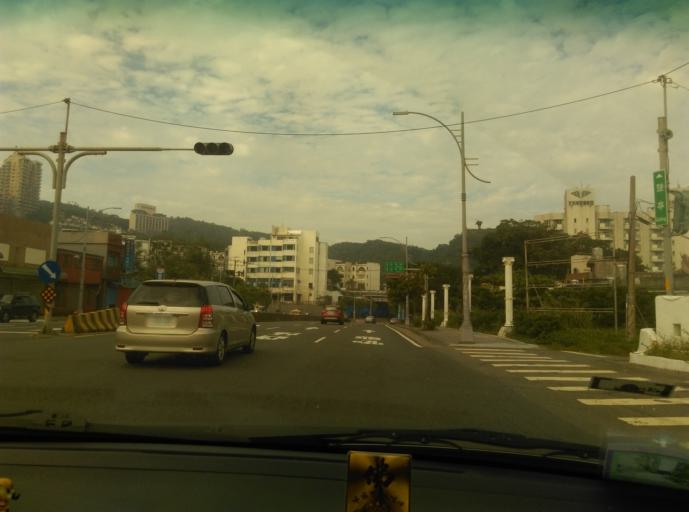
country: TW
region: Taiwan
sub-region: Keelung
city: Keelung
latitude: 25.1892
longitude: 121.6833
